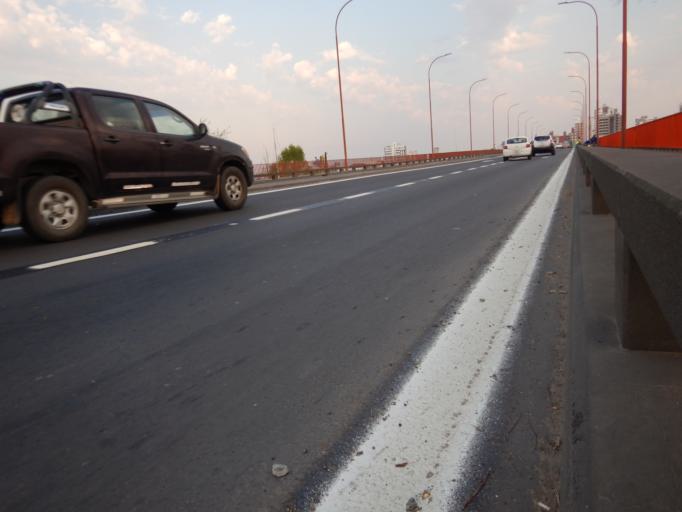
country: AR
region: Santa Fe
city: Santa Fe de la Vera Cruz
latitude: -31.6410
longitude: -60.6792
